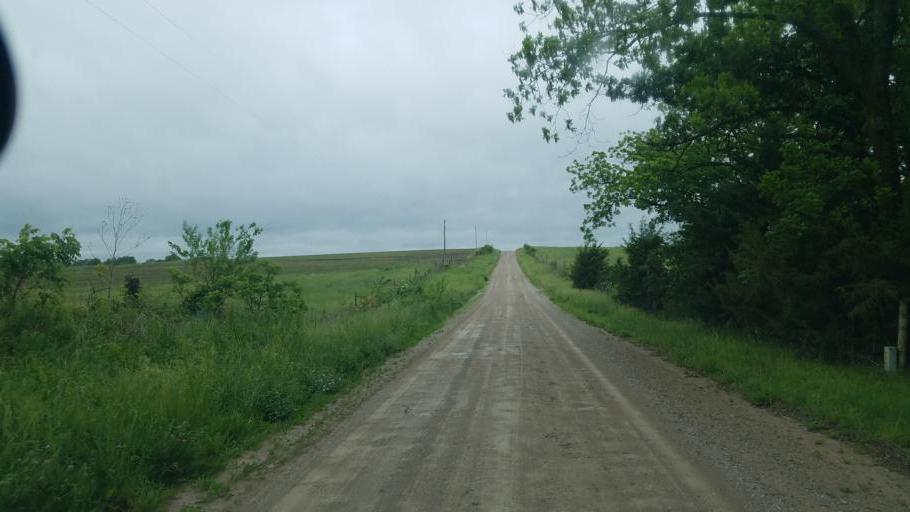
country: US
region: Missouri
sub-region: Carroll County
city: Carrollton
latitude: 39.4852
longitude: -93.4967
